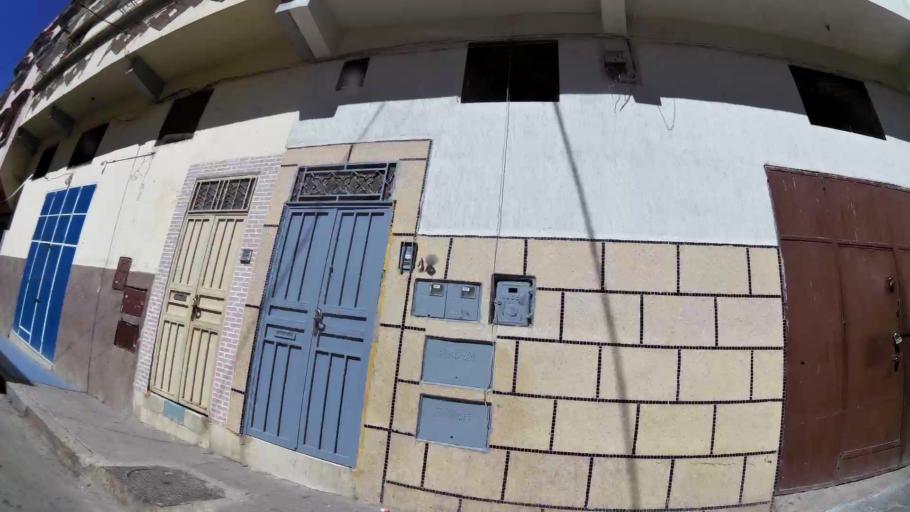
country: MA
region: Meknes-Tafilalet
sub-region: Meknes
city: Meknes
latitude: 33.8872
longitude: -5.5706
